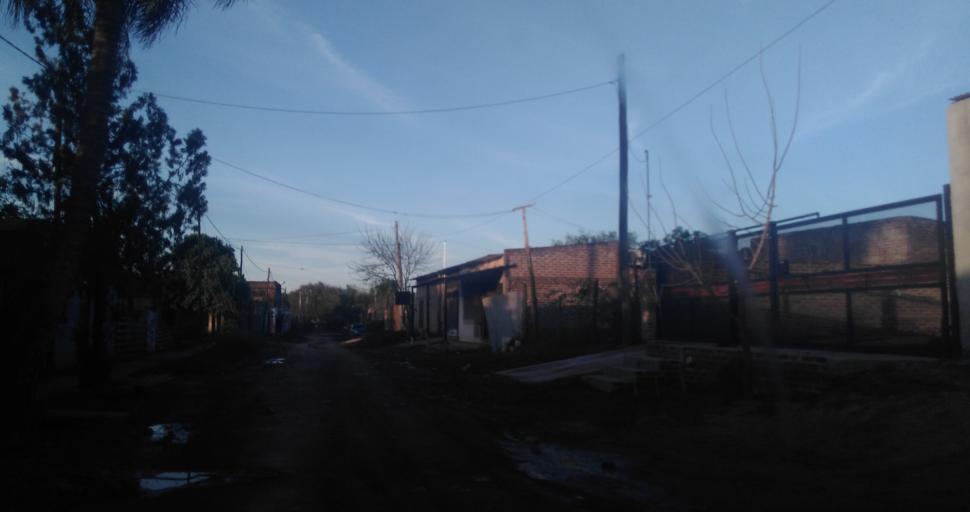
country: AR
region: Chaco
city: Fontana
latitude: -27.4286
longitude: -59.0007
